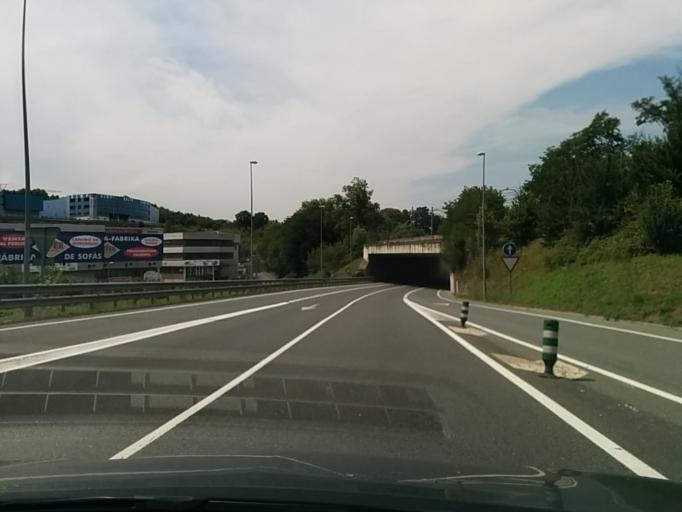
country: ES
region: Basque Country
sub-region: Provincia de Guipuzcoa
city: Lezo
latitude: 43.3193
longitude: -1.8686
